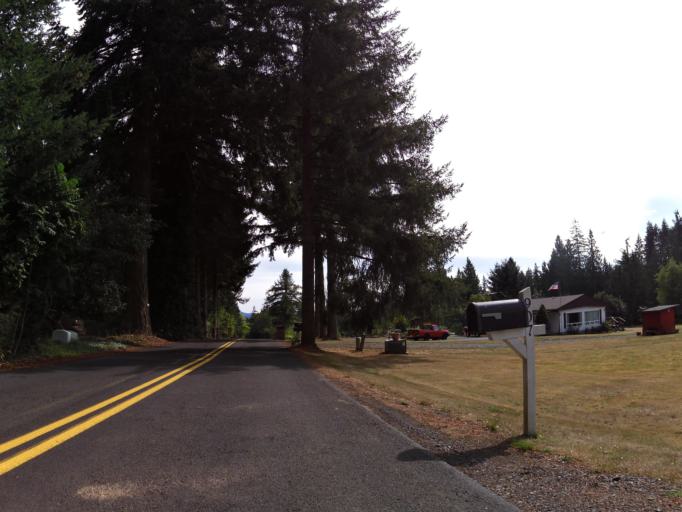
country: US
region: Washington
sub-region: Cowlitz County
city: Castle Rock
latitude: 46.3124
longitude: -122.9242
